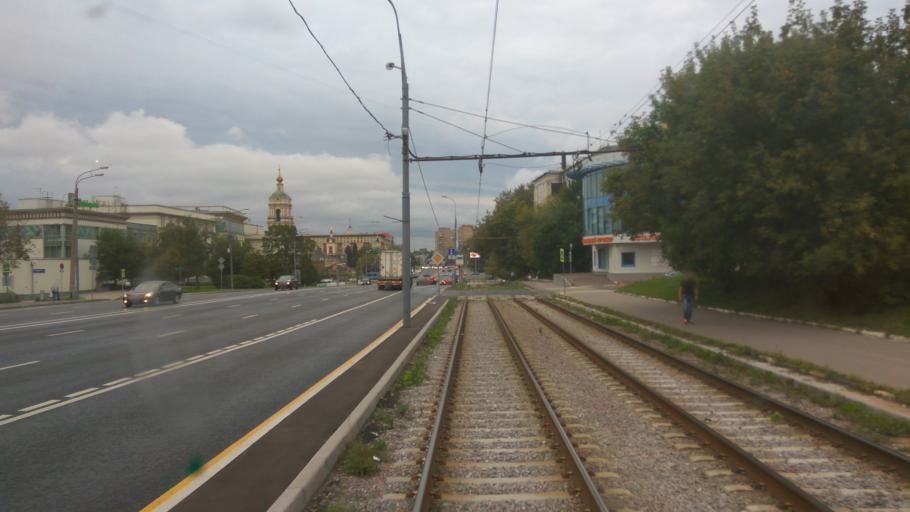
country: RU
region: Moscow
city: Taganskiy
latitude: 55.7280
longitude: 37.6628
